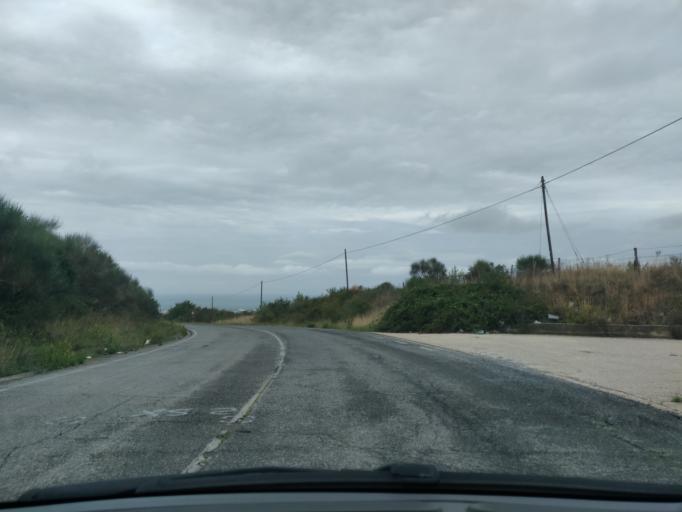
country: IT
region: Latium
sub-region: Citta metropolitana di Roma Capitale
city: Civitavecchia
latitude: 42.1123
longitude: 11.8463
